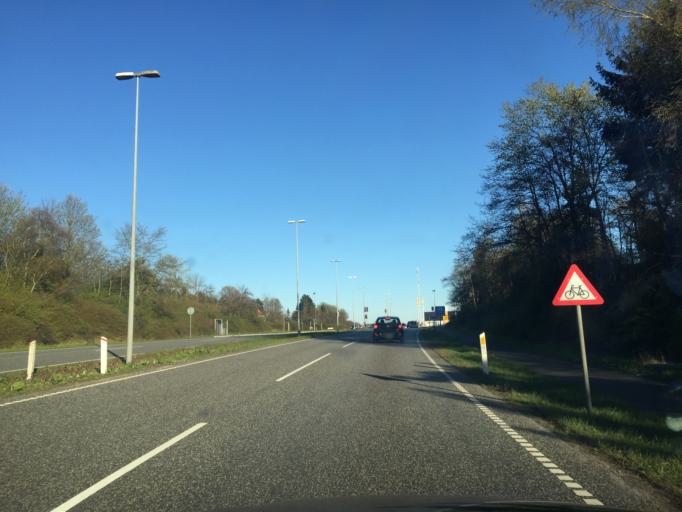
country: DK
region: Capital Region
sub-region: Egedal Kommune
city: Vekso
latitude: 55.7595
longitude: 12.2303
